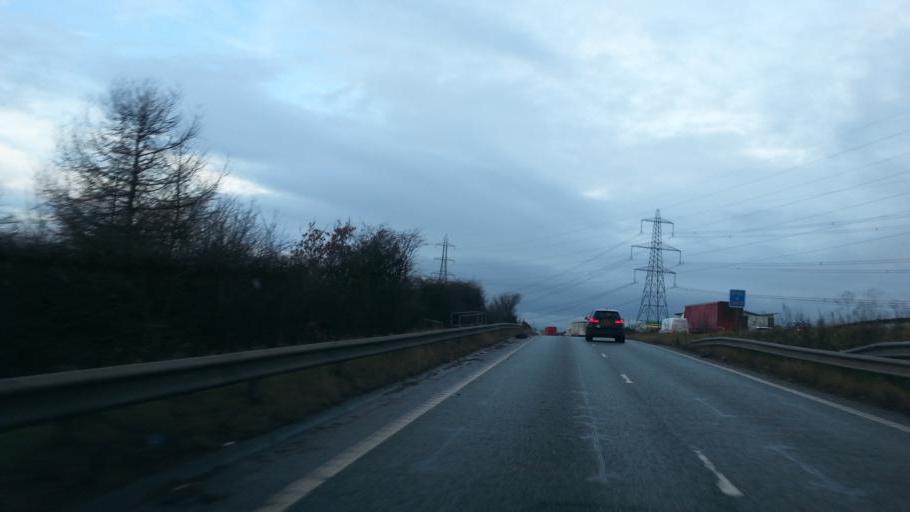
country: GB
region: England
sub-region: City and Borough of Wakefield
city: Pontefract
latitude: 53.7072
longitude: -1.3339
